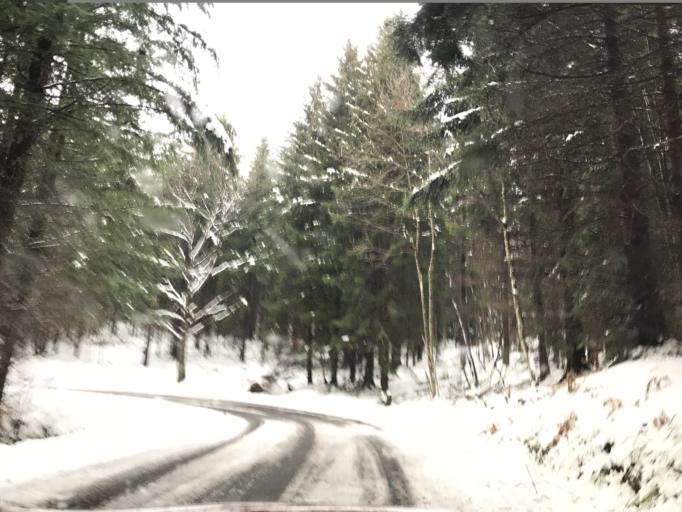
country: FR
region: Auvergne
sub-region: Departement du Puy-de-Dome
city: Celles-sur-Durolle
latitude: 45.7507
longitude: 3.6693
